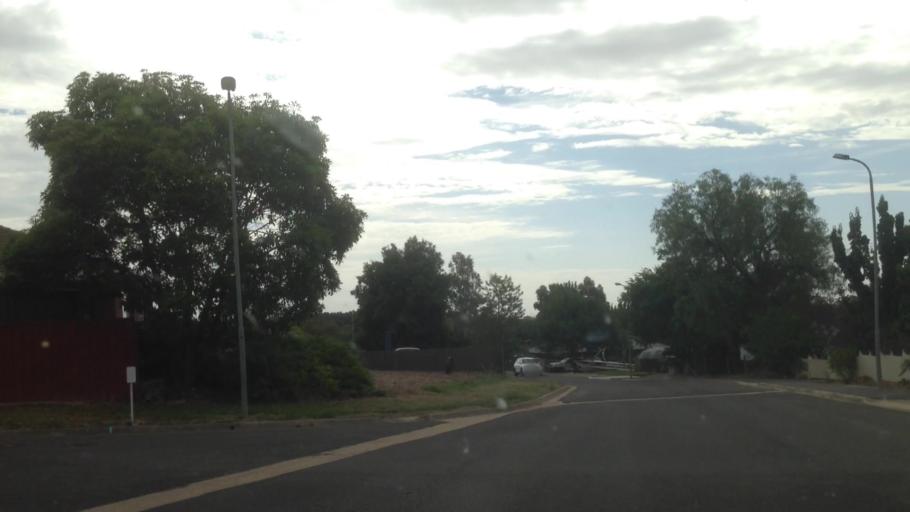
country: AU
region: South Australia
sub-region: Barossa
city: Williamstown
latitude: -34.6689
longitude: 138.8830
